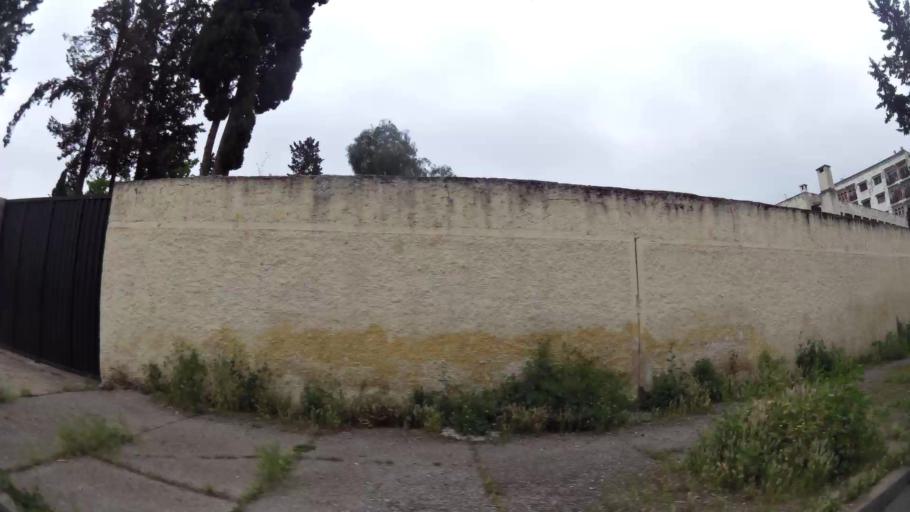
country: MA
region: Fes-Boulemane
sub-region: Fes
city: Fes
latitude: 34.0456
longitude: -4.9997
